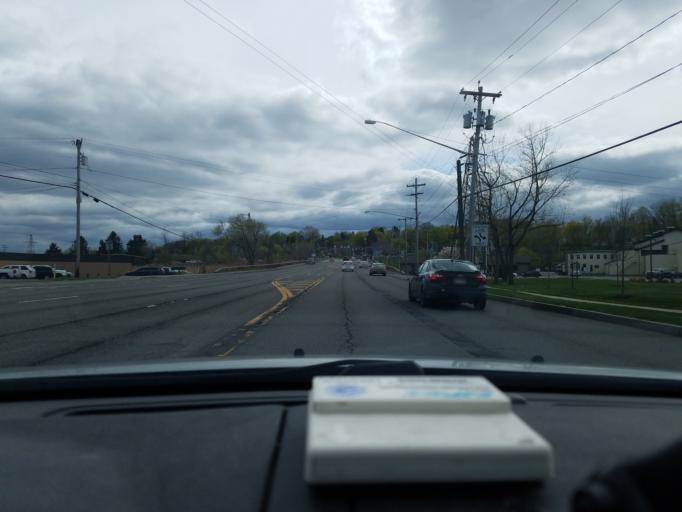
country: US
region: New York
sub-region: Onondaga County
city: East Syracuse
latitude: 43.0718
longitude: -76.0897
